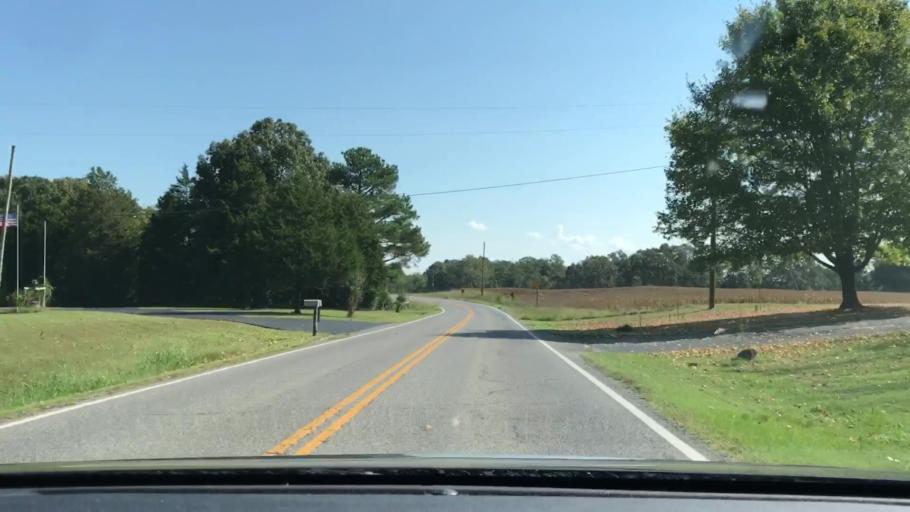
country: US
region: Kentucky
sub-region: Marshall County
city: Benton
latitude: 36.7638
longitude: -88.1980
